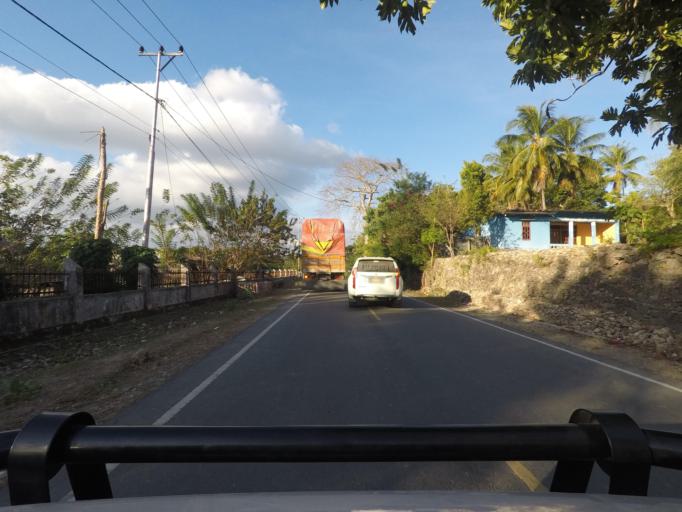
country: TL
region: Bobonaro
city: Maliana
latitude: -8.9691
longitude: 125.0445
